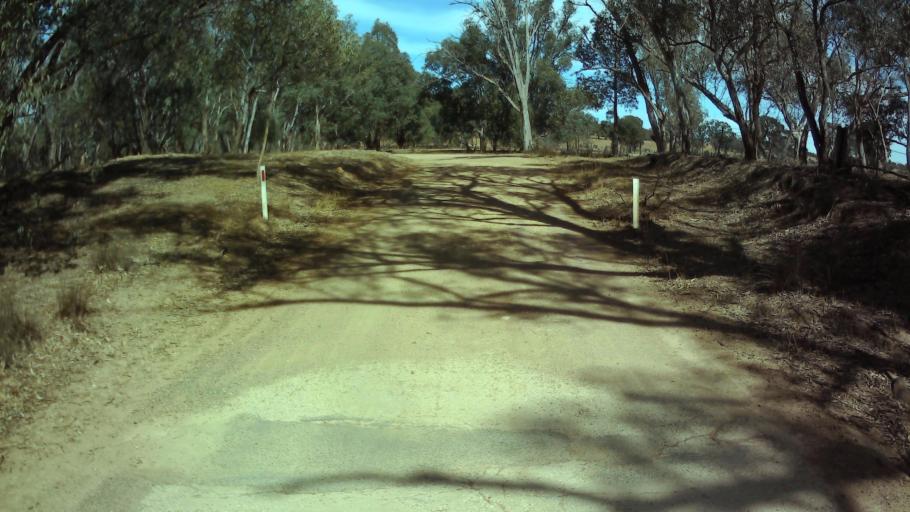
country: AU
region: New South Wales
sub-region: Weddin
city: Grenfell
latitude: -33.6841
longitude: 148.2806
